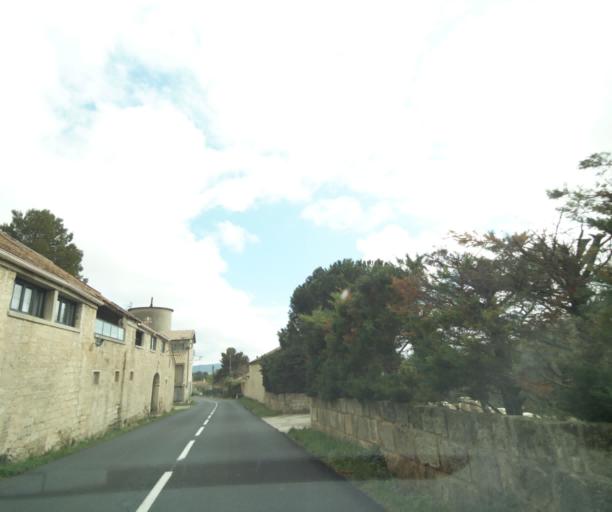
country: FR
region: Languedoc-Roussillon
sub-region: Departement de l'Herault
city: Pignan
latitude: 43.5862
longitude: 3.7555
